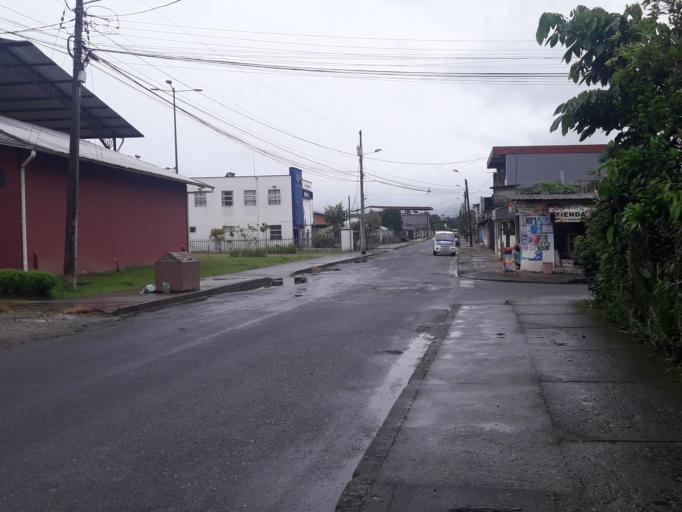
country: EC
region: Napo
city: Tena
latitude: -0.9860
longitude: -77.8183
